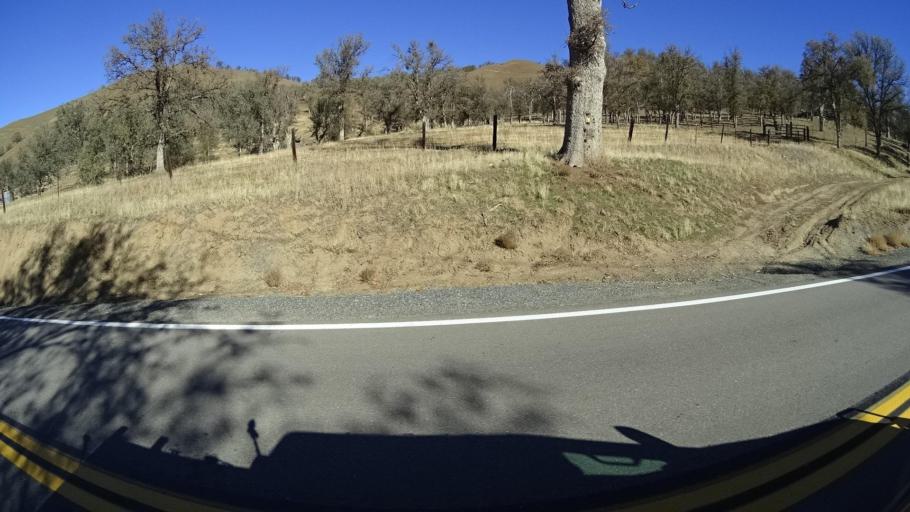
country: US
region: California
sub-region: Kern County
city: Alta Sierra
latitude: 35.7216
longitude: -118.6850
